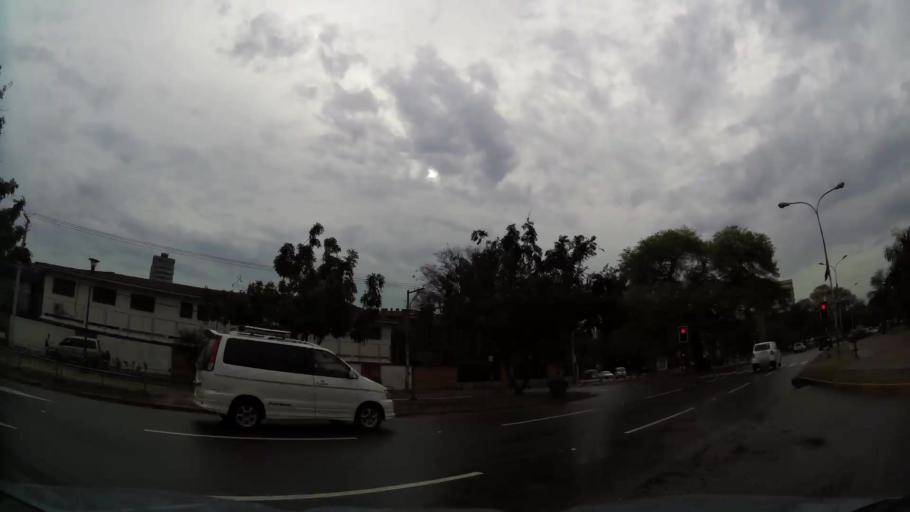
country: BO
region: Santa Cruz
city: Santa Cruz de la Sierra
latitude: -17.7946
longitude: -63.1744
